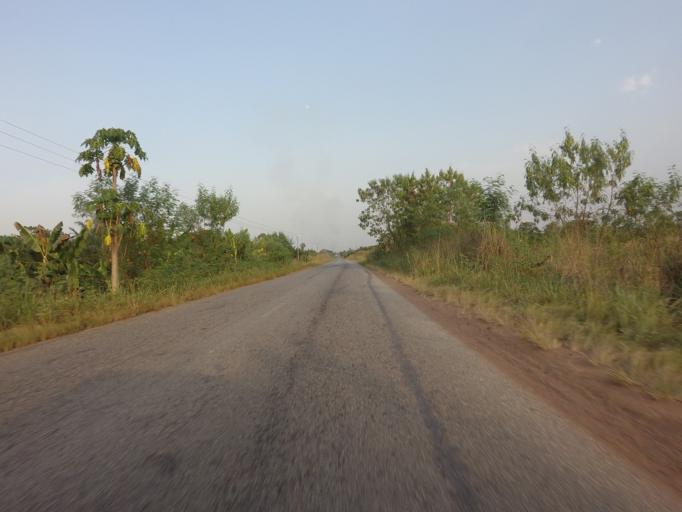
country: GH
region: Volta
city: Ho
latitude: 6.5732
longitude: 0.3701
